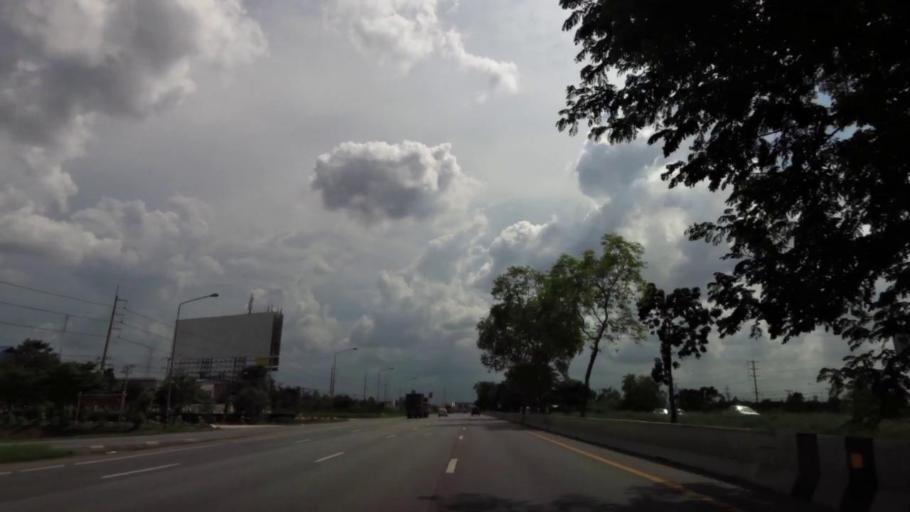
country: TH
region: Phra Nakhon Si Ayutthaya
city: Bang Pa-in
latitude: 14.2515
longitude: 100.6136
